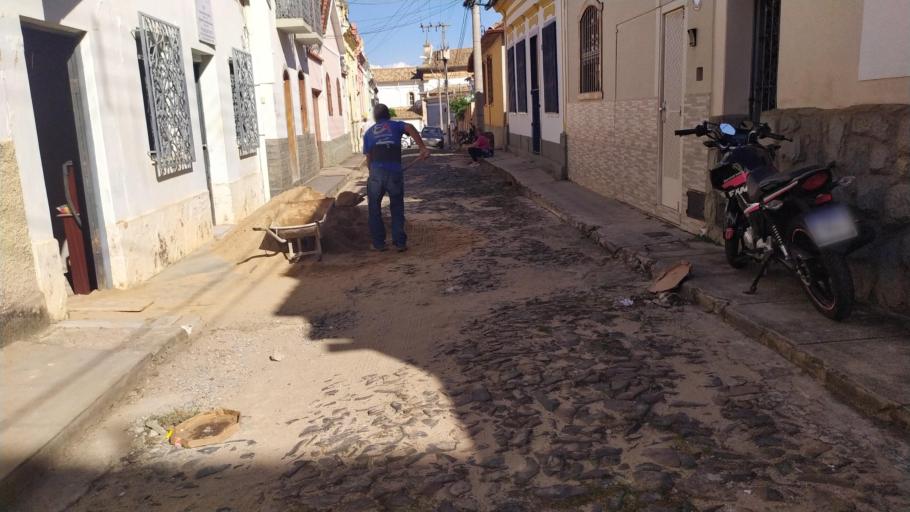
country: BR
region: Minas Gerais
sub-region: Sao Joao Del Rei
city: Sao Joao del Rei
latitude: -21.1328
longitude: -44.2620
